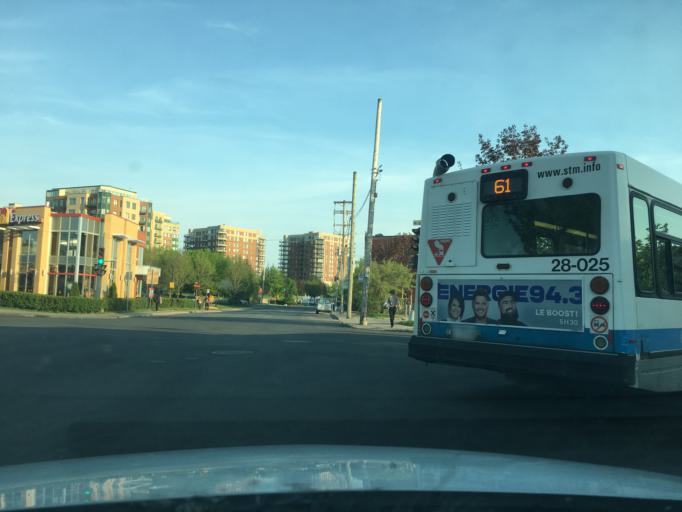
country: CA
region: Quebec
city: Westmount
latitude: 45.4629
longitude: -73.5637
